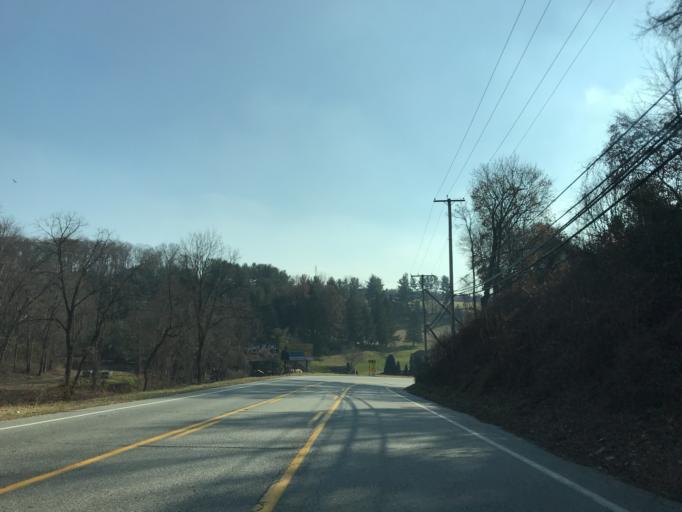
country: US
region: Pennsylvania
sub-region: York County
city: Jacobus
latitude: 39.9067
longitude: -76.7133
